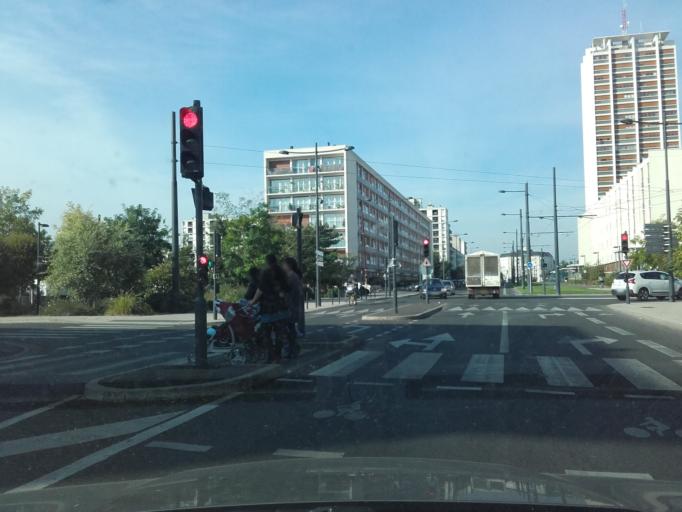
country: FR
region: Centre
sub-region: Departement d'Indre-et-Loire
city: Tours
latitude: 47.3806
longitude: 0.6980
